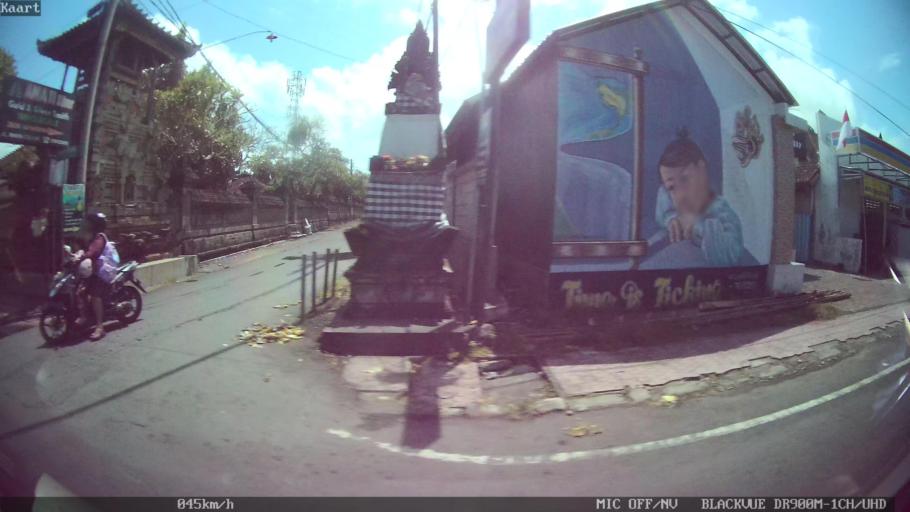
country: ID
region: Bali
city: Banjar Pasekan
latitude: -8.6033
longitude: 115.2773
